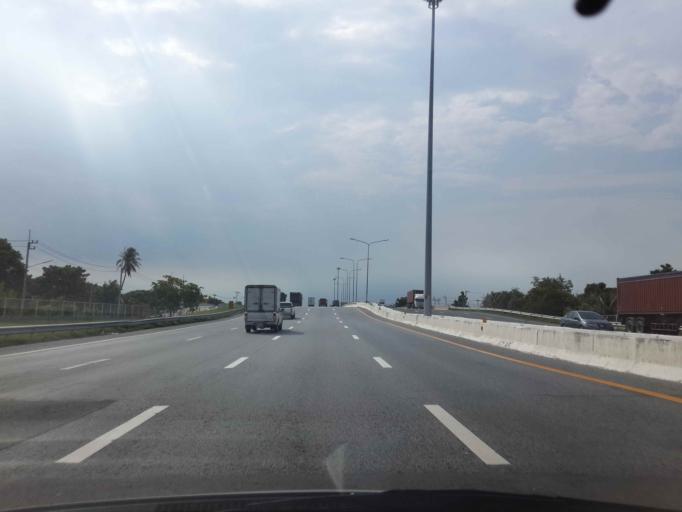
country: TH
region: Chachoengsao
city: Bang Pakong
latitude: 13.6090
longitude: 100.9387
